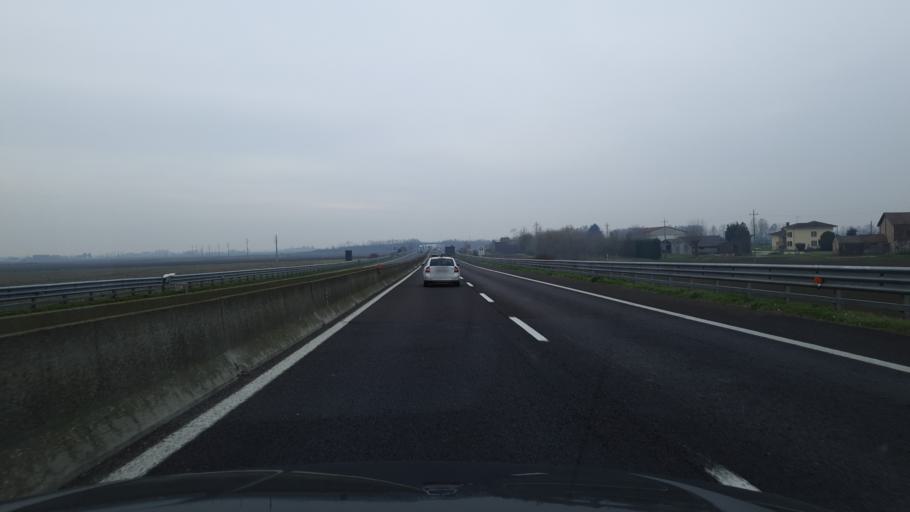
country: IT
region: Veneto
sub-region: Provincia di Rovigo
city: Villamarzana
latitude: 45.0030
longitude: 11.6772
